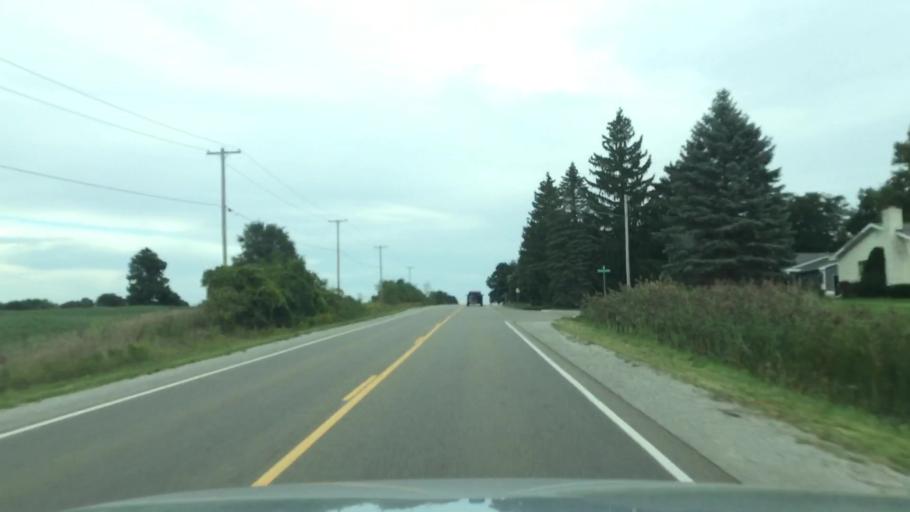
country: US
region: Michigan
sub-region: Genesee County
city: Lake Fenton
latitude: 42.8858
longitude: -83.6882
